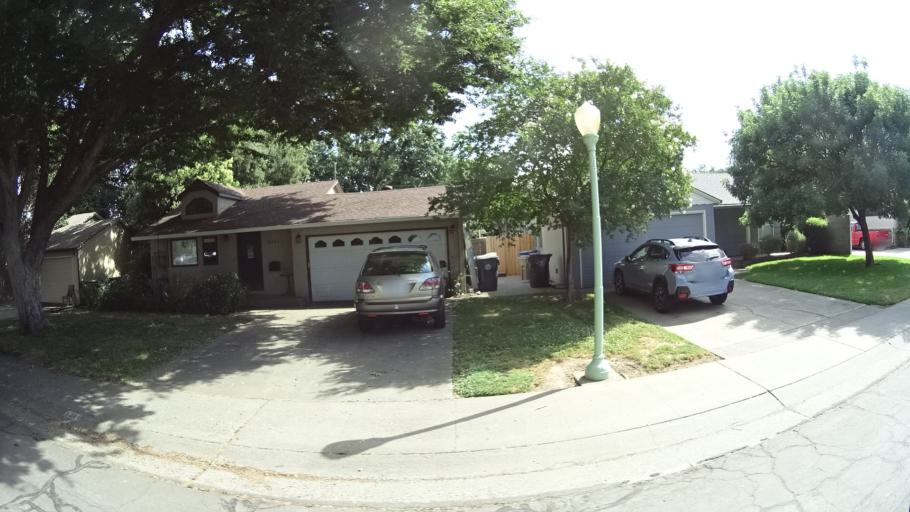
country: US
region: California
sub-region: Sacramento County
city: Arden-Arcade
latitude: 38.5775
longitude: -121.4306
